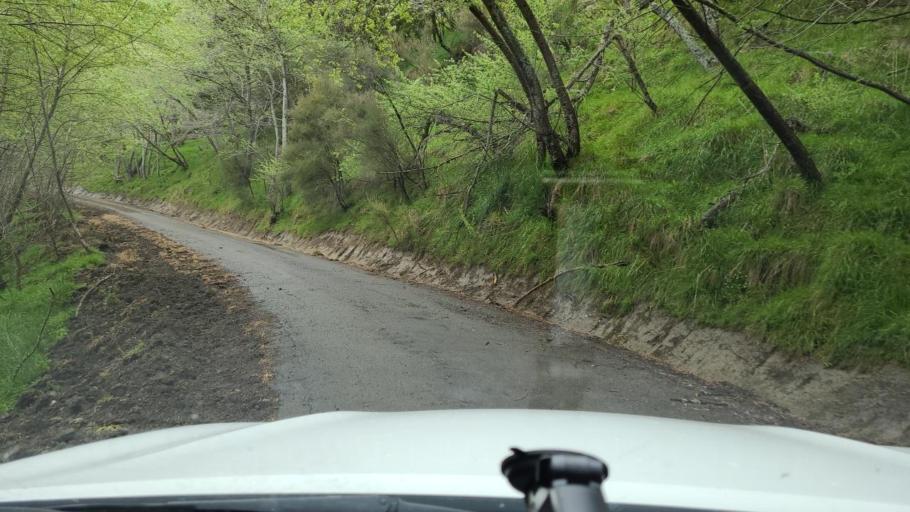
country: NZ
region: Gisborne
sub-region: Gisborne District
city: Gisborne
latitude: -38.4306
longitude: 177.7155
